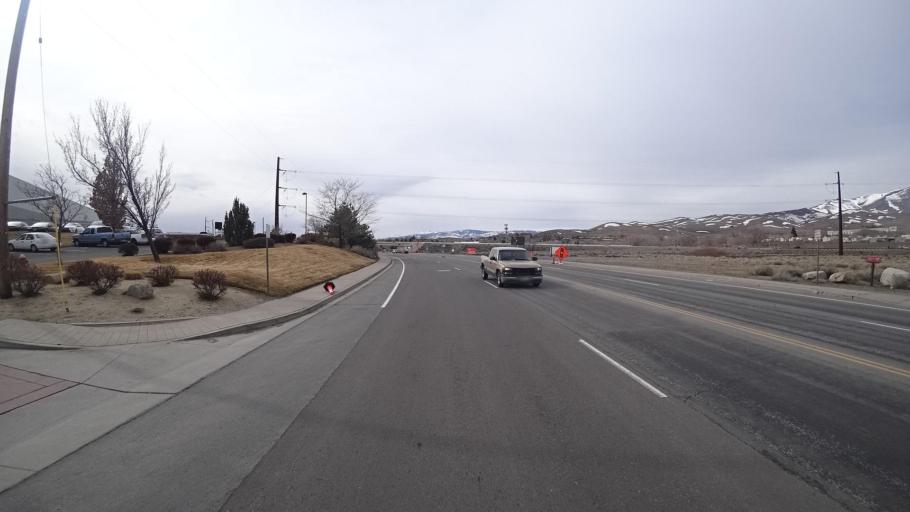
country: US
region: Nevada
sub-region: Washoe County
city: Golden Valley
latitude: 39.6028
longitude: -119.8369
